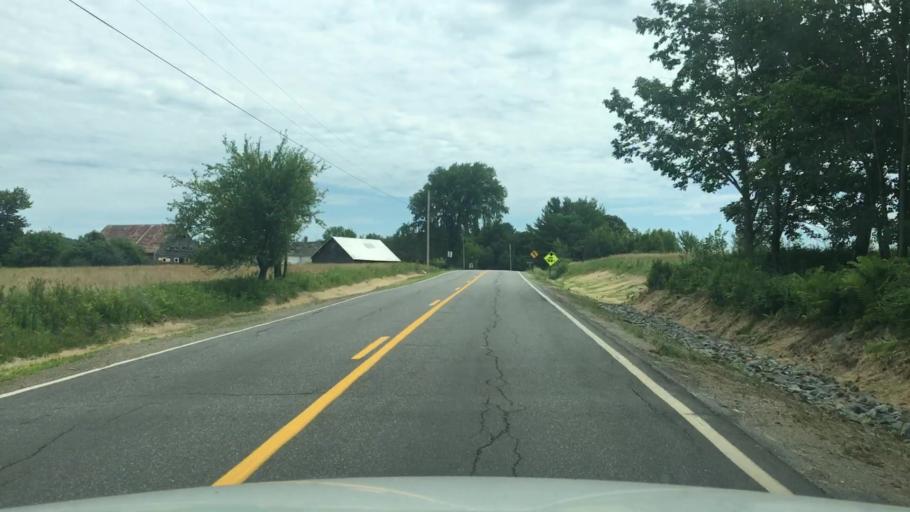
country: US
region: Maine
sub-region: Waldo County
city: Searsmont
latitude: 44.4570
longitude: -69.2650
